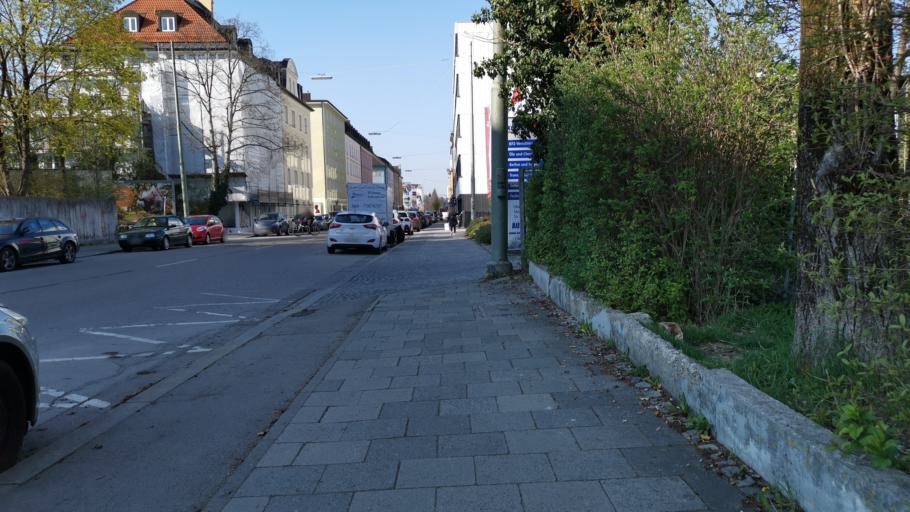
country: DE
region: Bavaria
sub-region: Upper Bavaria
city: Pullach im Isartal
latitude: 48.0982
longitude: 11.5286
